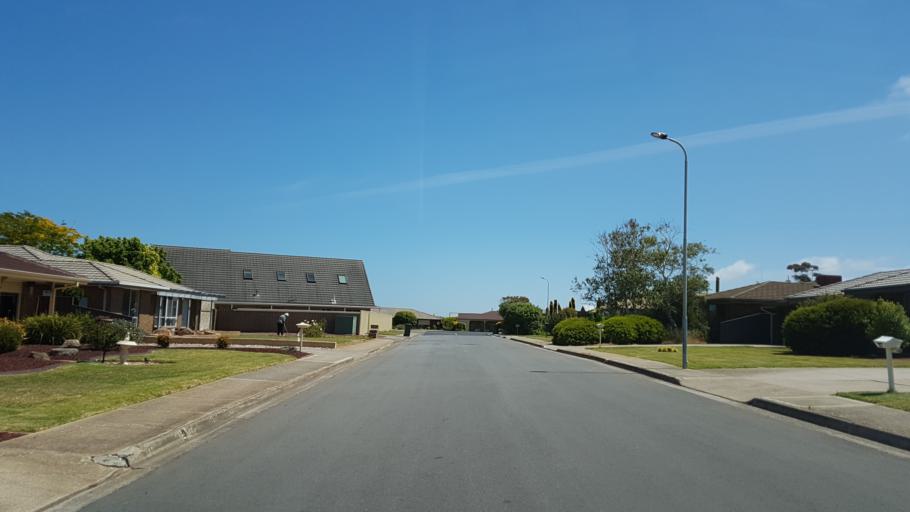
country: AU
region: South Australia
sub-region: Marion
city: Marino
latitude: -35.0642
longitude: 138.5153
